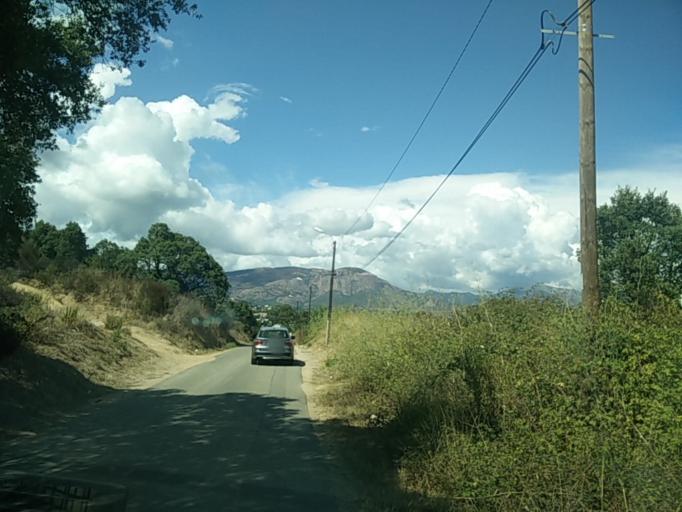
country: FR
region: Corsica
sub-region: Departement de la Corse-du-Sud
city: Ajaccio
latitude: 41.9472
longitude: 8.7722
